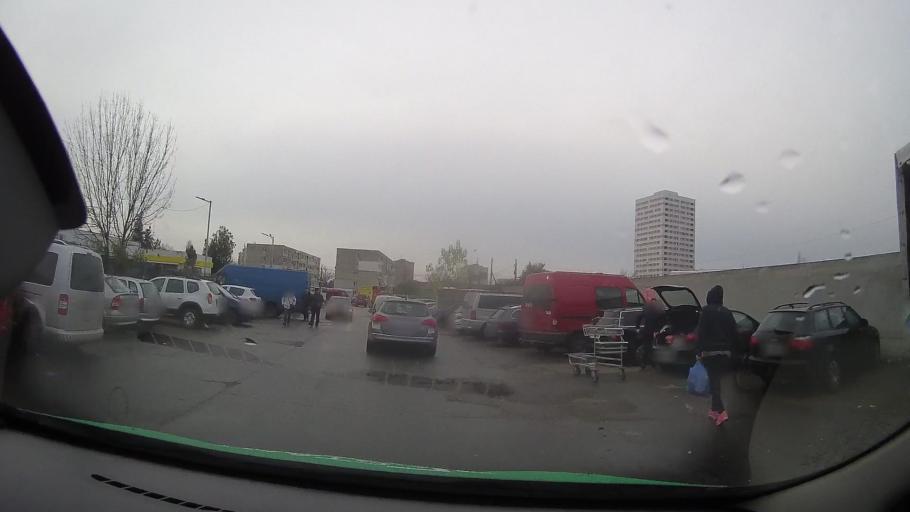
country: RO
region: Prahova
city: Ploiesti
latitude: 44.9414
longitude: 25.9903
